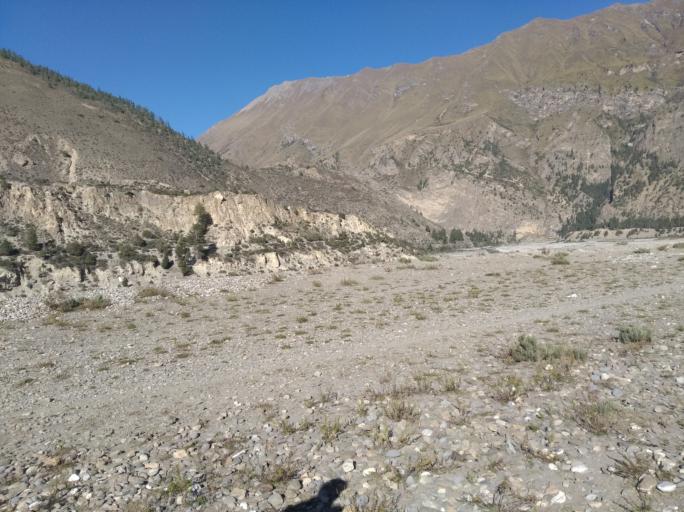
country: NP
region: Western Region
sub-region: Dhawalagiri Zone
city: Jomsom
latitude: 28.8915
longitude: 83.1911
